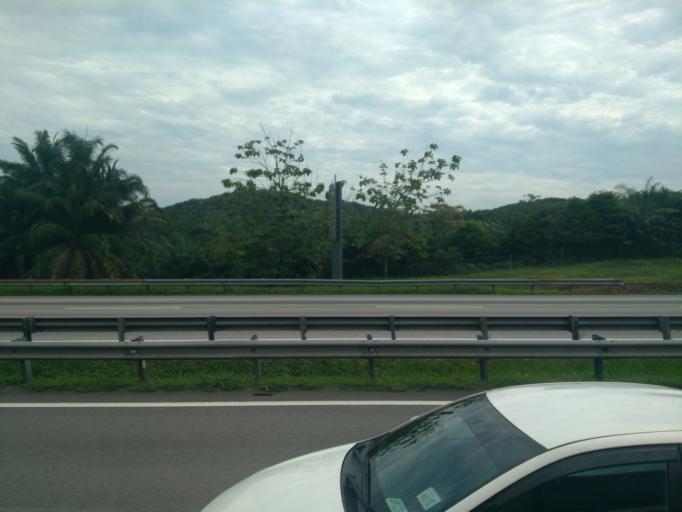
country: MY
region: Negeri Sembilan
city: Seremban
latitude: 2.6586
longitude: 101.9863
